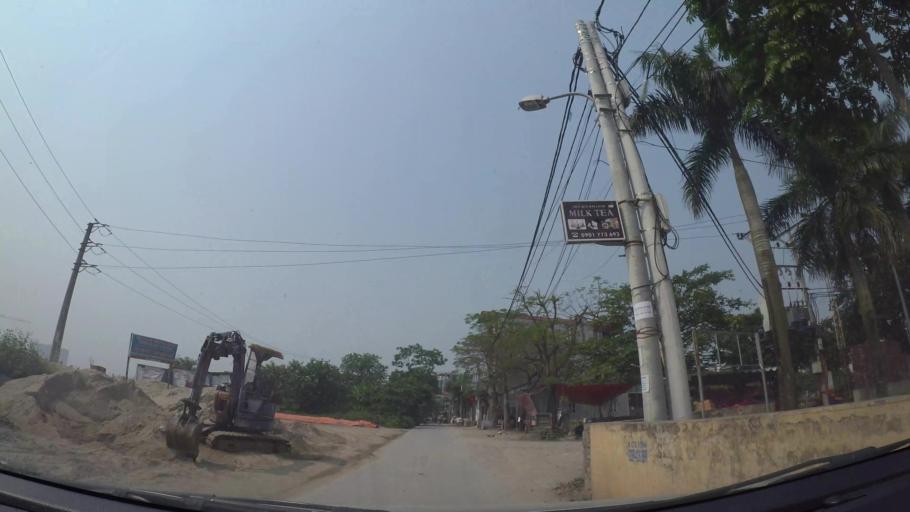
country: VN
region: Ha Noi
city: Cau Dien
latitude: 21.0031
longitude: 105.7586
